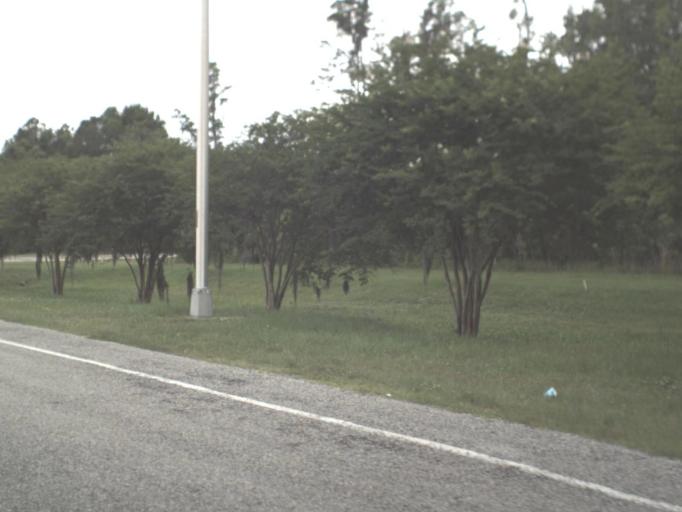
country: US
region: Florida
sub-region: Duval County
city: Jacksonville
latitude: 30.4751
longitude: -81.6645
